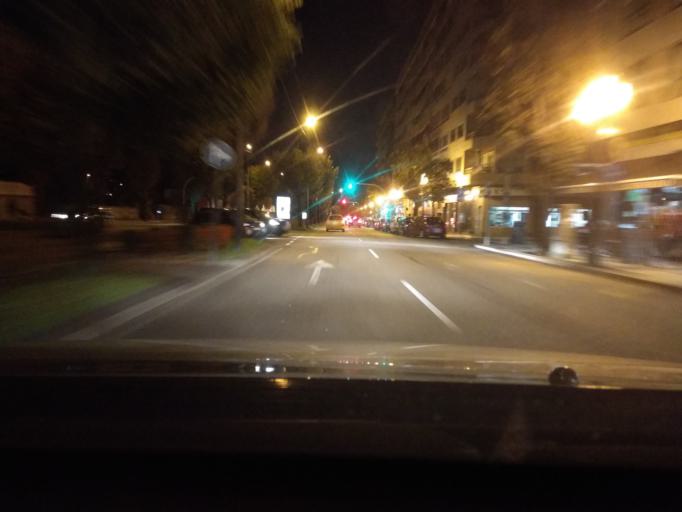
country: ES
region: Galicia
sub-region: Provincia de Pontevedra
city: Vigo
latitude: 42.2238
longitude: -8.7239
